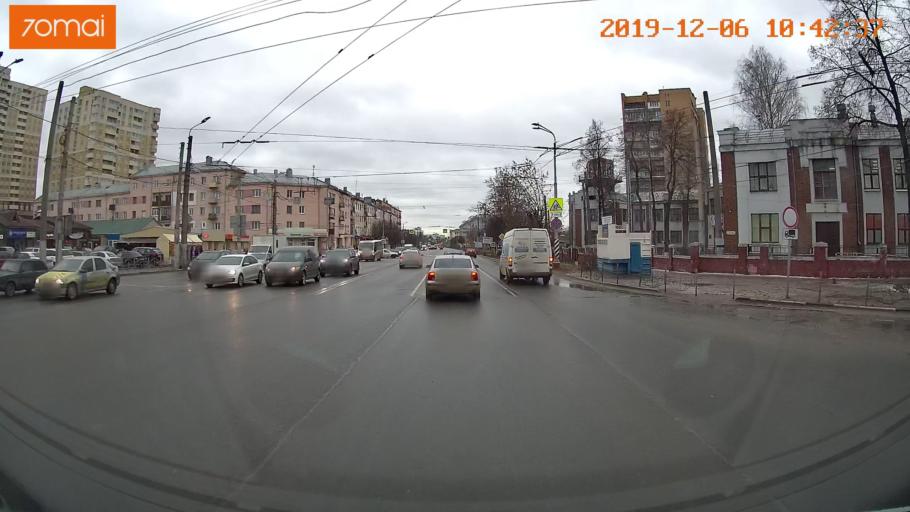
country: RU
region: Ivanovo
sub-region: Gorod Ivanovo
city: Ivanovo
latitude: 57.0170
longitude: 40.9693
